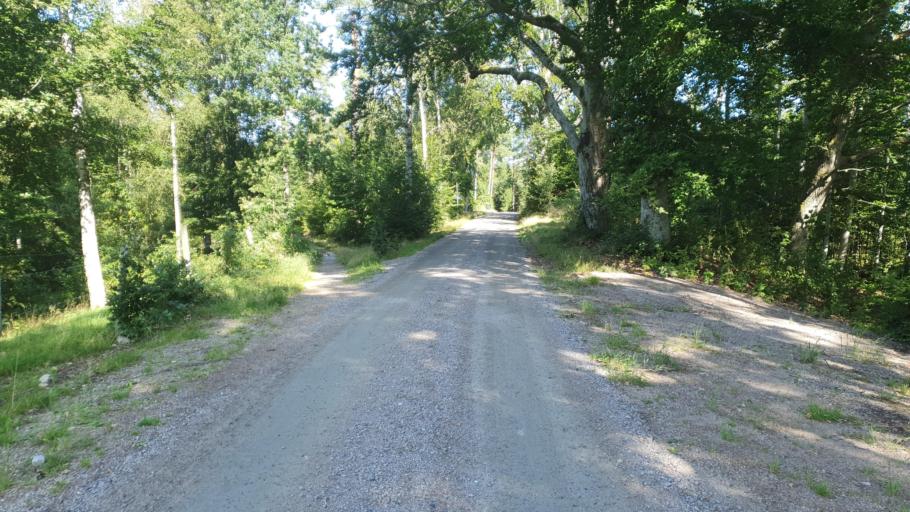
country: SE
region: Kronoberg
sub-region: Vaxjo Kommun
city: Vaexjoe
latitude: 56.9822
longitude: 14.7676
